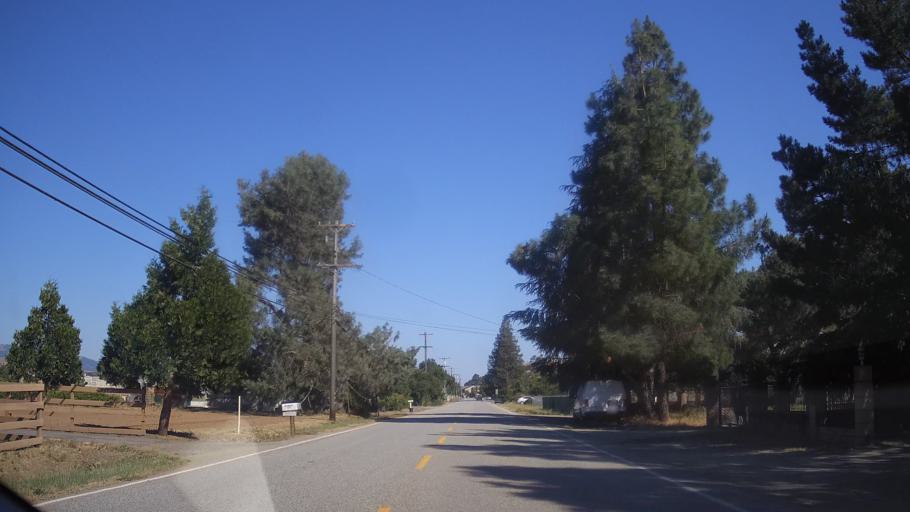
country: US
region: California
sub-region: Santa Clara County
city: Morgan Hill
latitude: 37.1565
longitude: -121.6825
